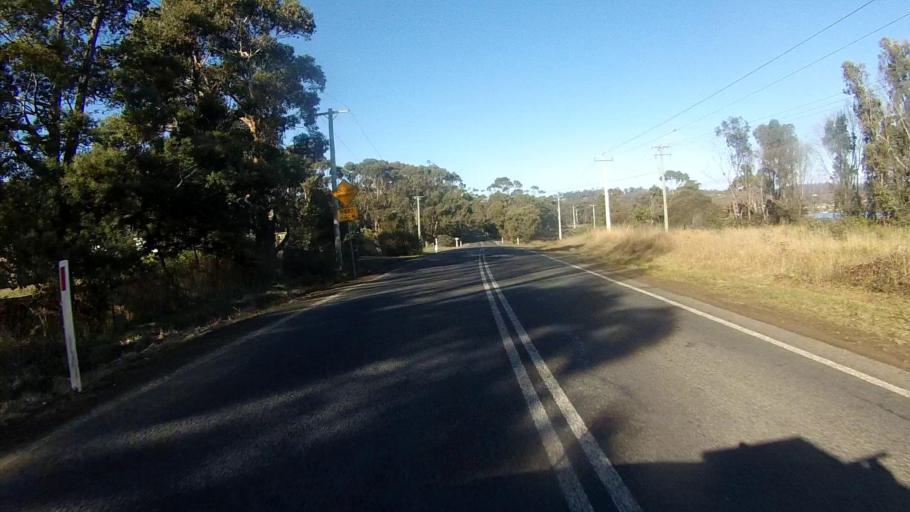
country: AU
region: Tasmania
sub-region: Sorell
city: Sorell
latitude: -42.9337
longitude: 147.8562
